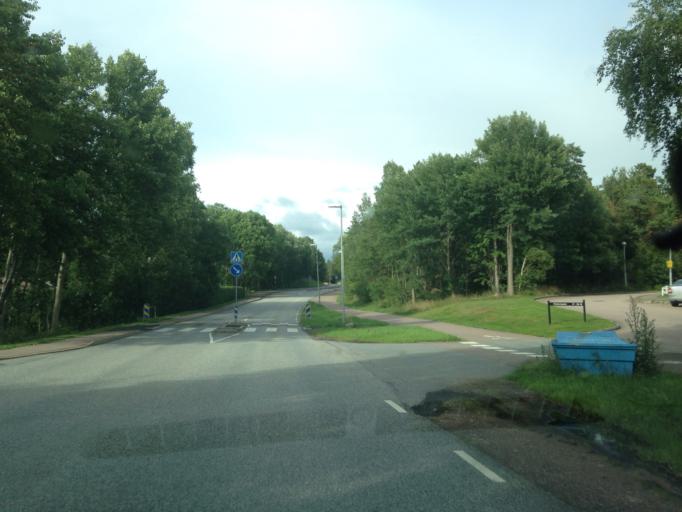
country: SE
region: Vaestra Goetaland
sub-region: Goteborg
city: Goeteborg
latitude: 57.7603
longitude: 11.9663
